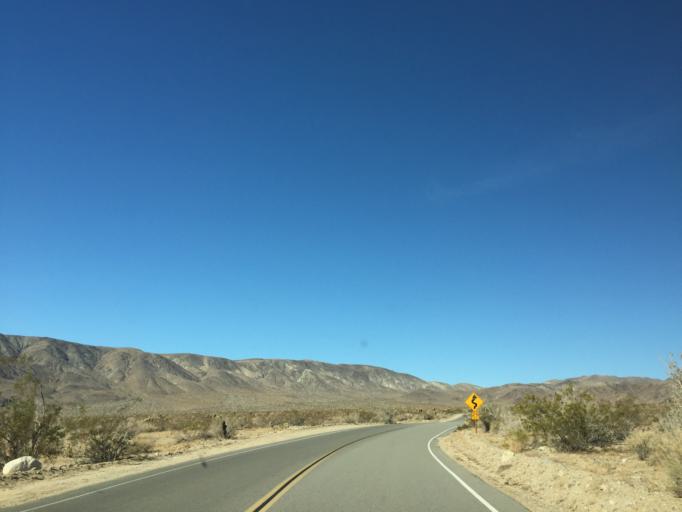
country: US
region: California
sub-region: San Bernardino County
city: Twentynine Palms
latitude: 33.9240
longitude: -115.9196
